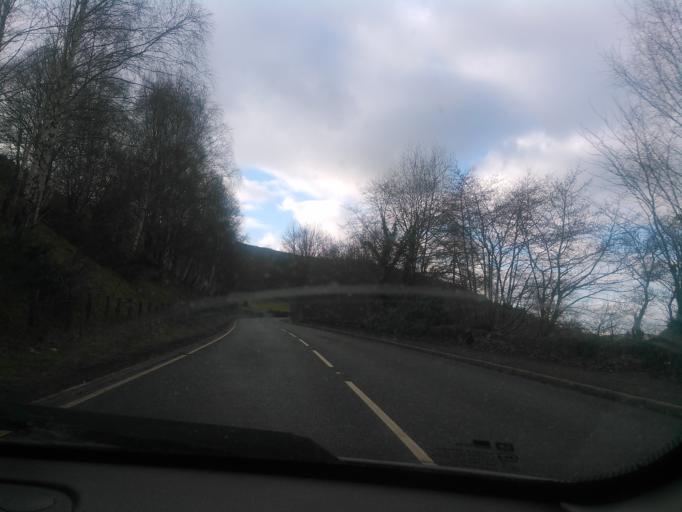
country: GB
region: Wales
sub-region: Denbighshire
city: Corwen
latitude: 52.9783
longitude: -3.3248
